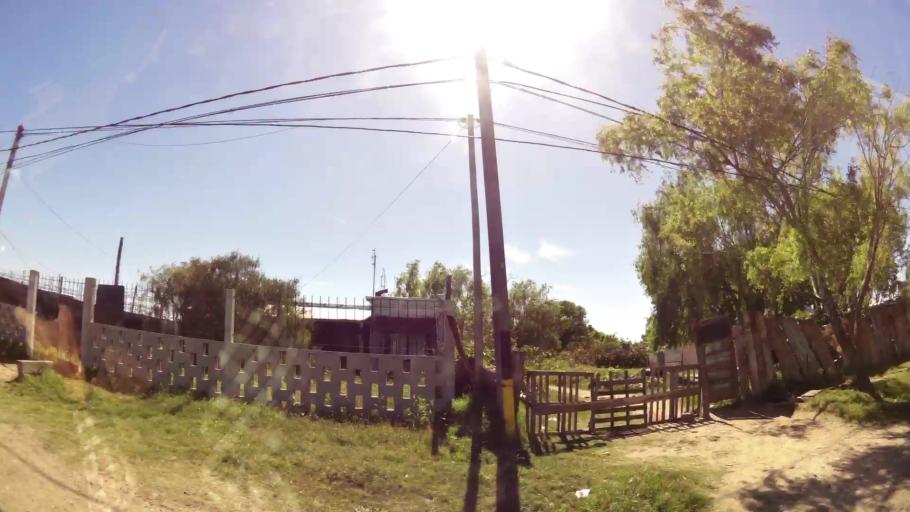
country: UY
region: Canelones
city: Paso de Carrasco
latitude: -34.8631
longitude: -56.1115
